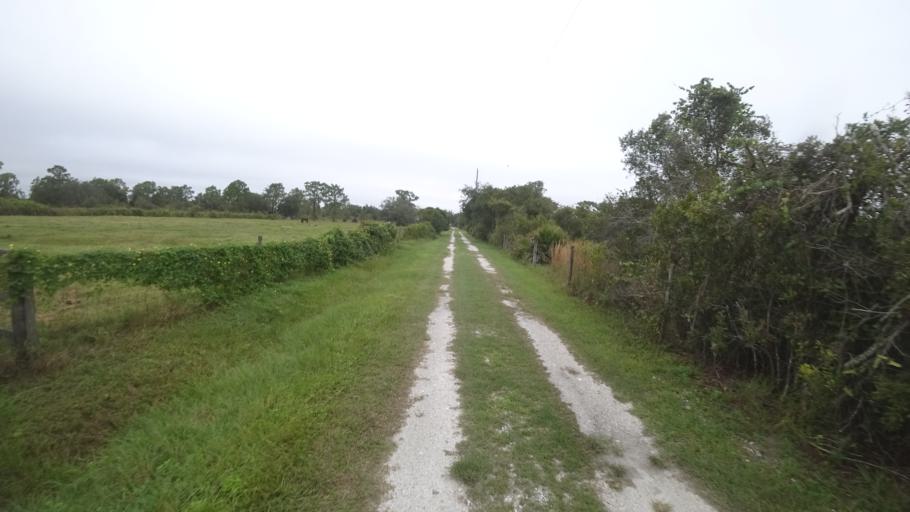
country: US
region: Florida
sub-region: Sarasota County
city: Warm Mineral Springs
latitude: 27.2754
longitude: -82.1327
